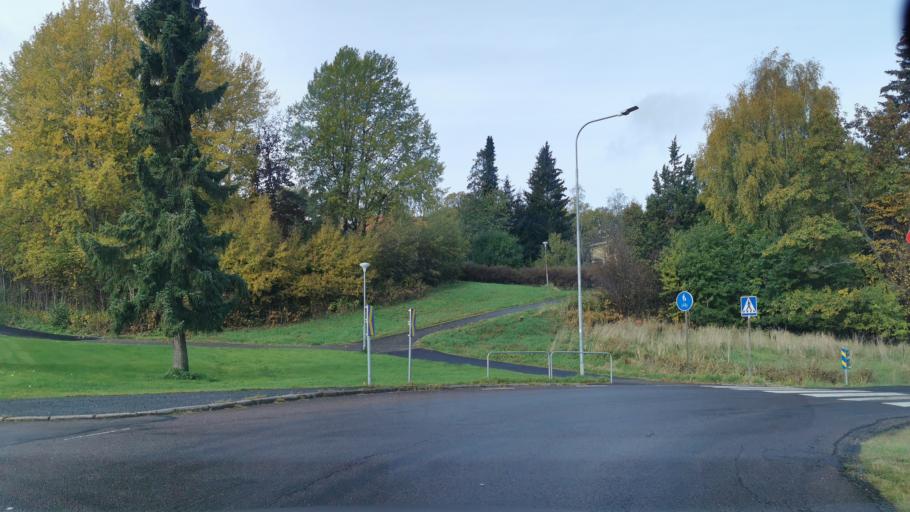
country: SE
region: Vaestra Goetaland
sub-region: Partille Kommun
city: Partille
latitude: 57.7320
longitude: 12.0888
